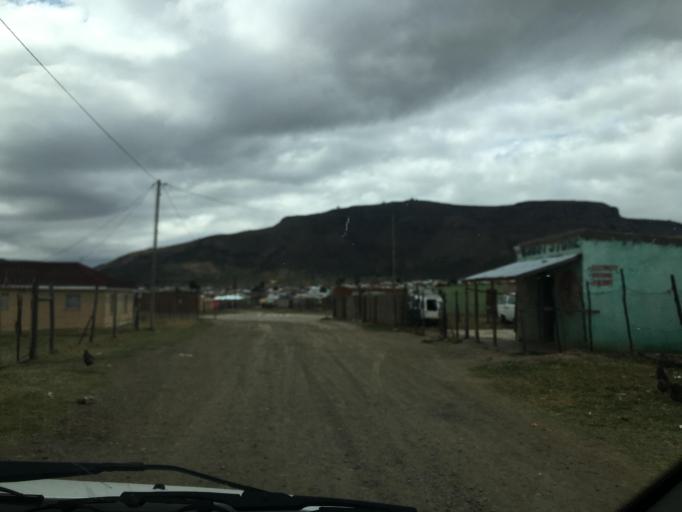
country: ZA
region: Eastern Cape
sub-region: Chris Hani District Municipality
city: Cala
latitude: -31.5392
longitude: 27.6998
